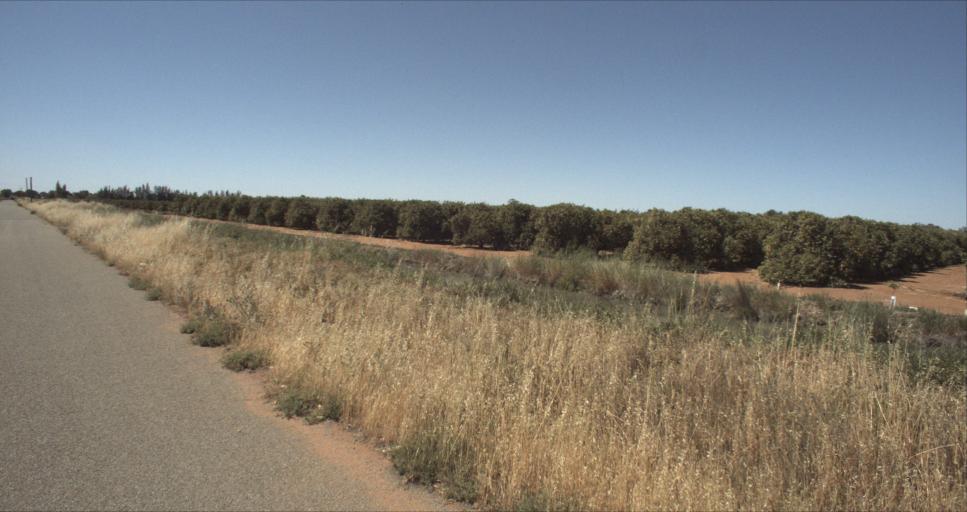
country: AU
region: New South Wales
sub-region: Leeton
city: Leeton
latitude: -34.5375
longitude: 146.3521
